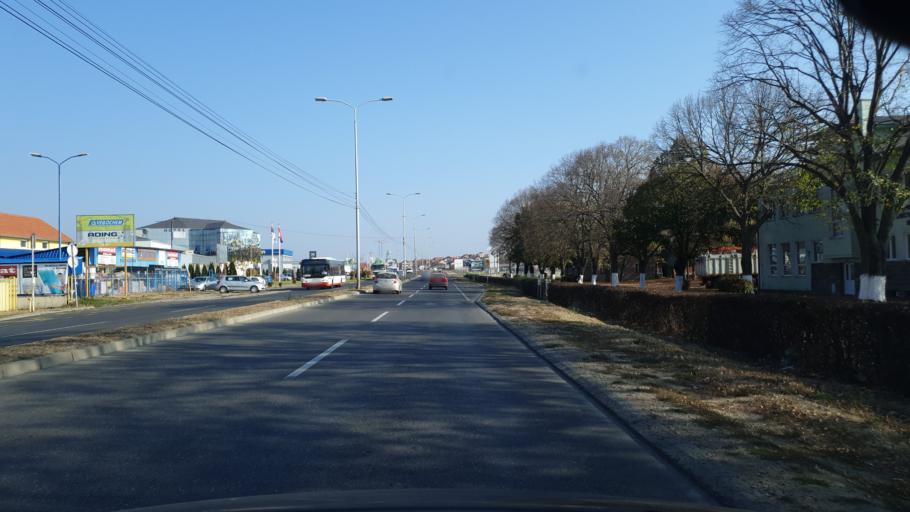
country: RS
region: Central Serbia
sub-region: Nisavski Okrug
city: Nis
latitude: 43.3166
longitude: 21.8468
